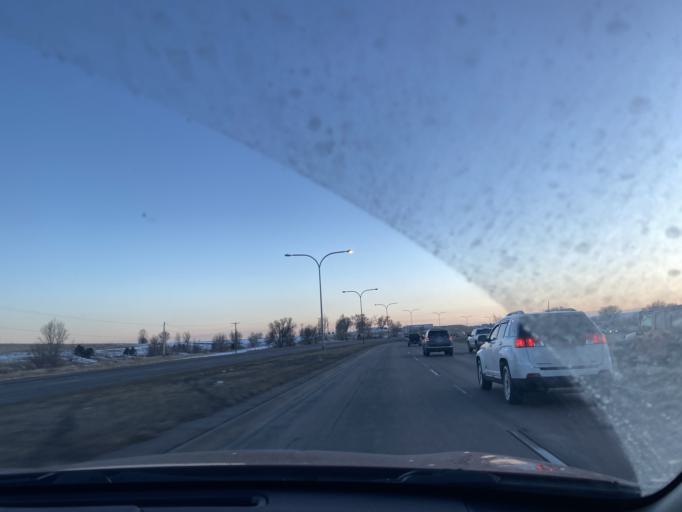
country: US
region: Colorado
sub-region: El Paso County
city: Cimarron Hills
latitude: 38.8333
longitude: -104.7209
